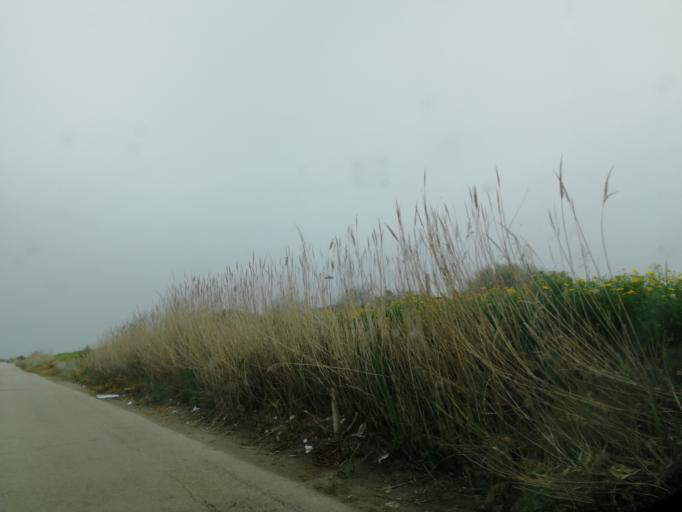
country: IT
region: Apulia
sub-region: Provincia di Barletta - Andria - Trani
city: Barletta
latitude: 41.3190
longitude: 16.3019
